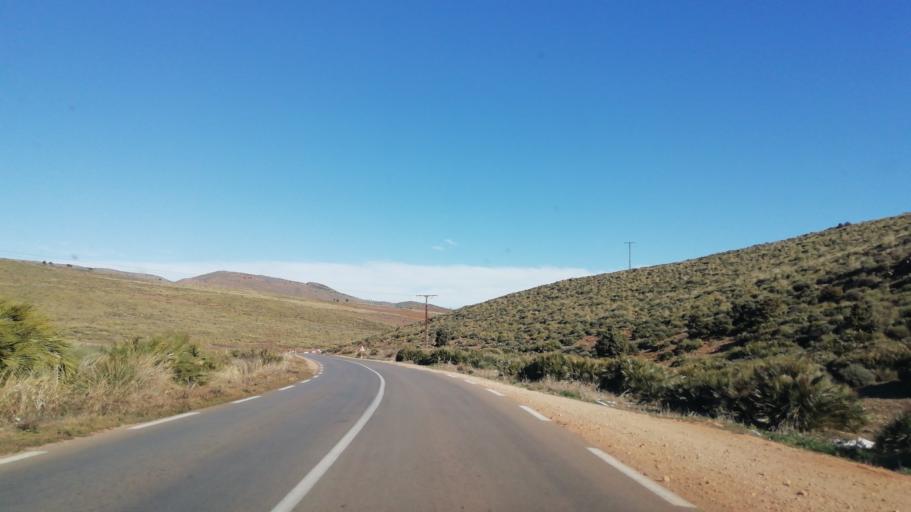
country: DZ
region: Tlemcen
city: Ouled Mimoun
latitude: 34.7690
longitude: -1.1363
